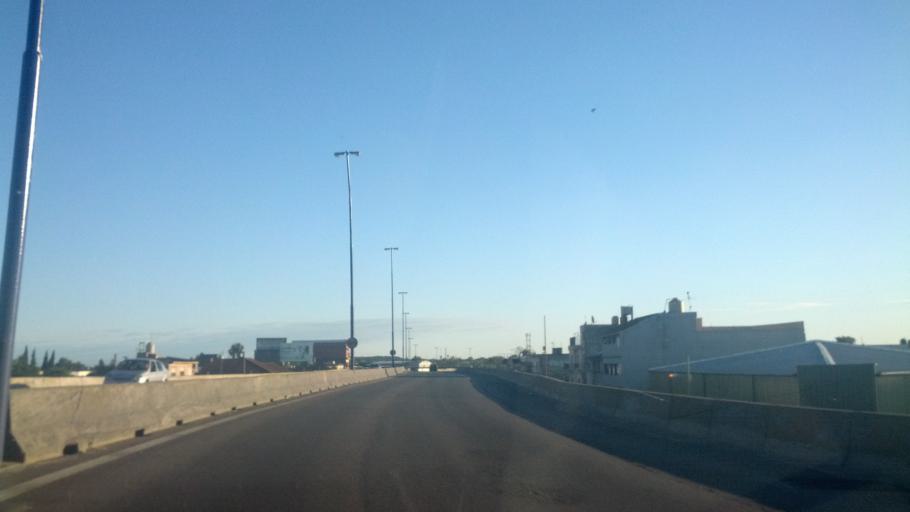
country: AR
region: Buenos Aires
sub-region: Partido de Lomas de Zamora
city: Lomas de Zamora
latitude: -34.7440
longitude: -58.4295
